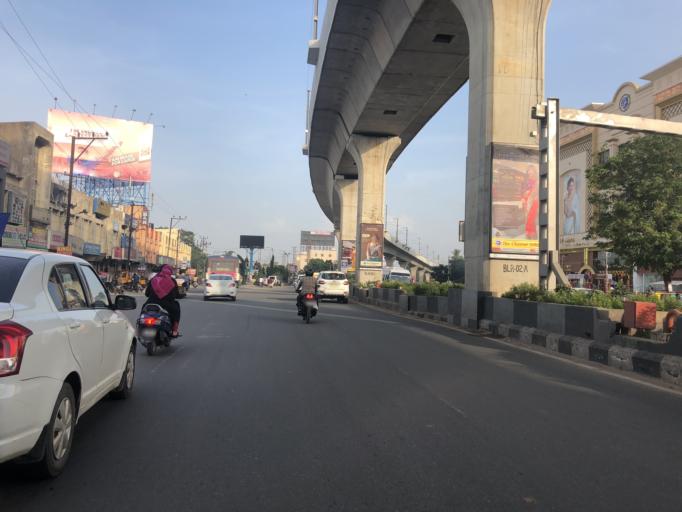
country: IN
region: Telangana
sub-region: Rangareddi
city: Kukatpalli
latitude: 17.4765
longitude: 78.4226
